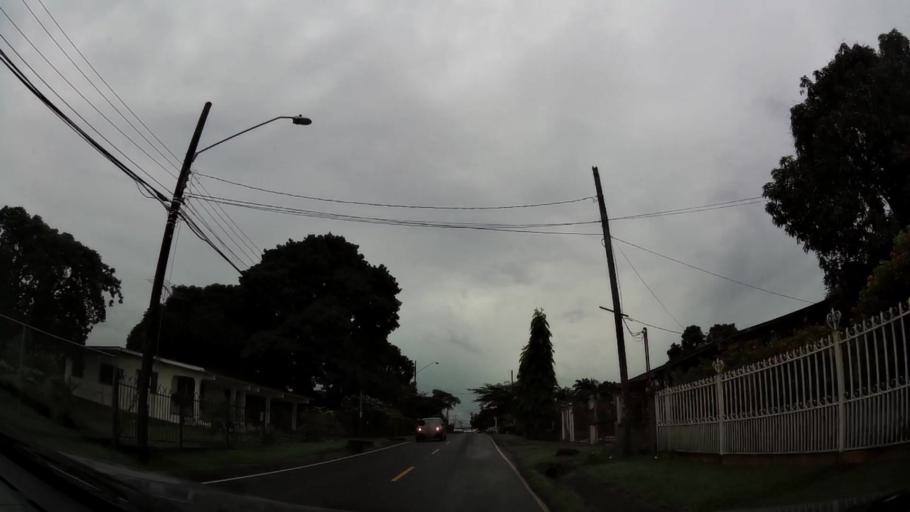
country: PA
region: Veraguas
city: Santiago de Veraguas
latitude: 8.1105
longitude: -80.9761
